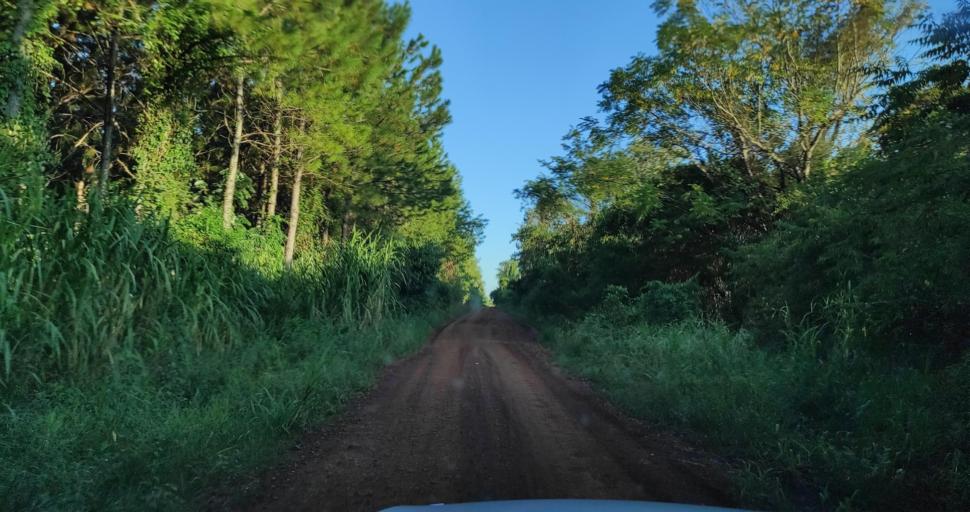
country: AR
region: Misiones
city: Gobernador Roca
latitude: -27.2191
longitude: -55.4377
